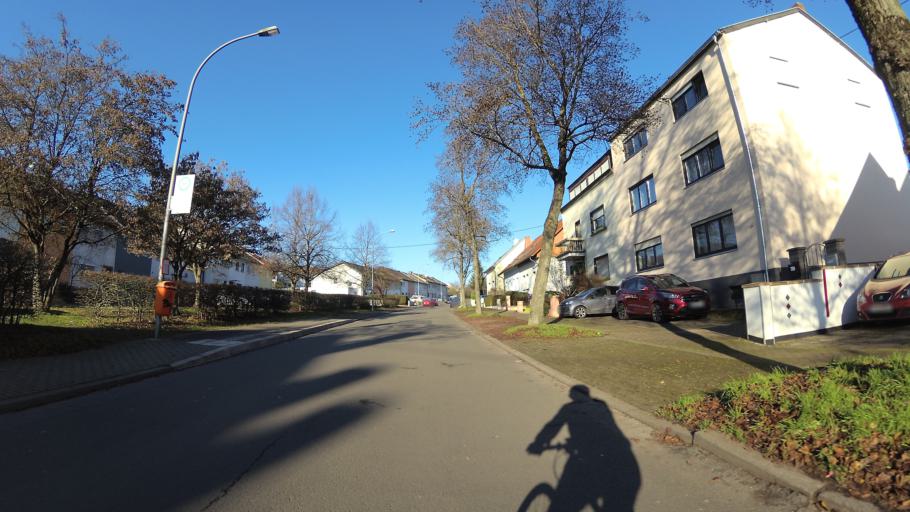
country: DE
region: Saarland
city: Saarlouis
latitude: 49.3360
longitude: 6.7525
